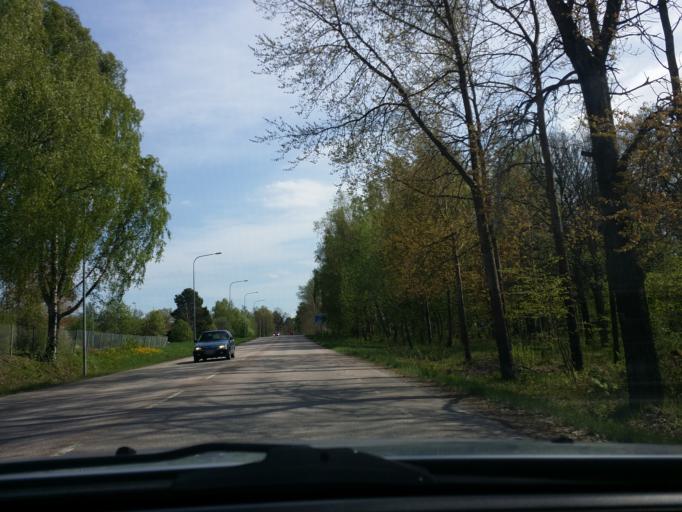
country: SE
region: Vaestmanland
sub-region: Vasteras
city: Vasteras
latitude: 59.6037
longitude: 16.5860
